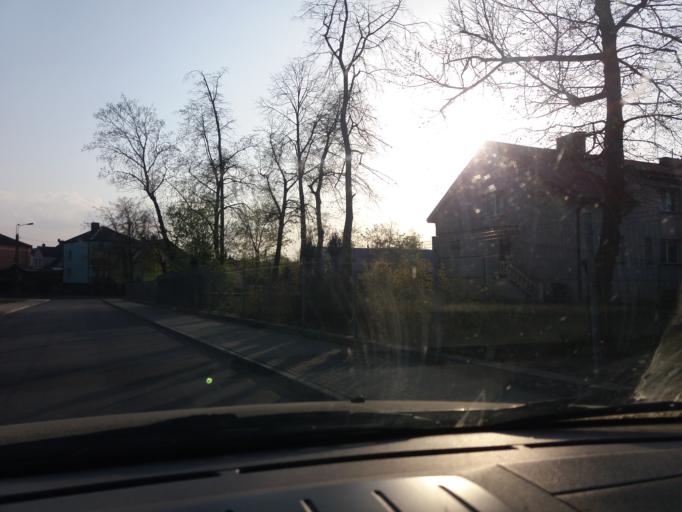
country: PL
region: Masovian Voivodeship
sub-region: Powiat mlawski
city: Mlawa
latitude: 53.1271
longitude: 20.3568
